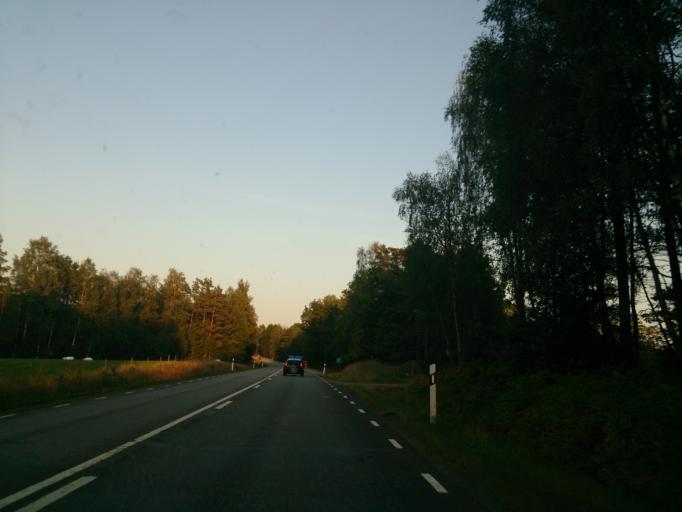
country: SE
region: Kronoberg
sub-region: Alvesta Kommun
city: Alvesta
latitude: 56.9081
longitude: 14.4309
